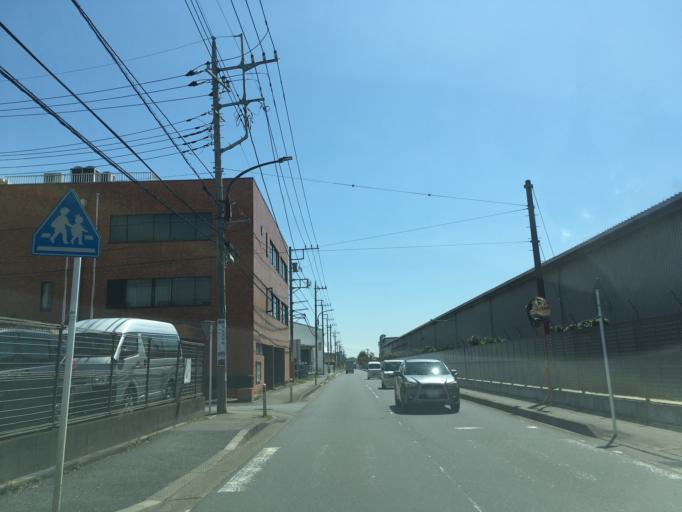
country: JP
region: Tokyo
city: Hachioji
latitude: 35.5671
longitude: 139.3358
